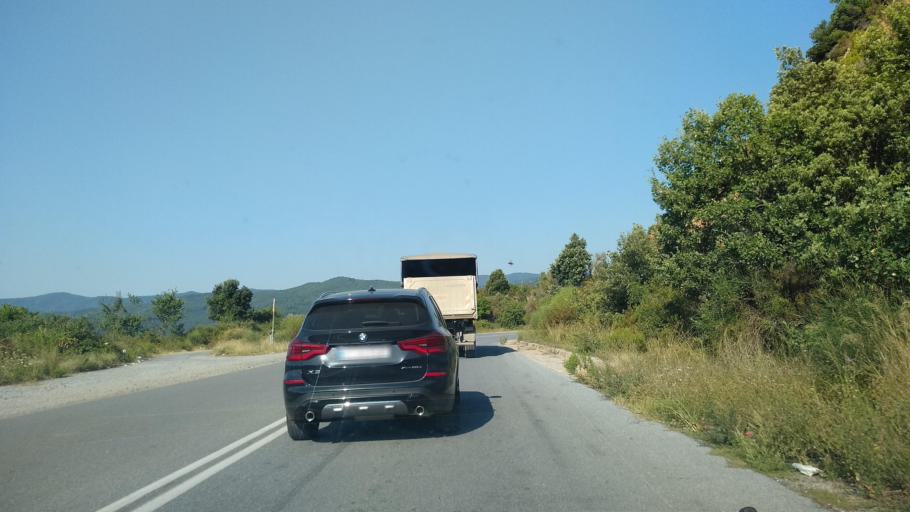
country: GR
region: Central Macedonia
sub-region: Nomos Chalkidikis
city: Stratonion
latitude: 40.5191
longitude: 23.8151
